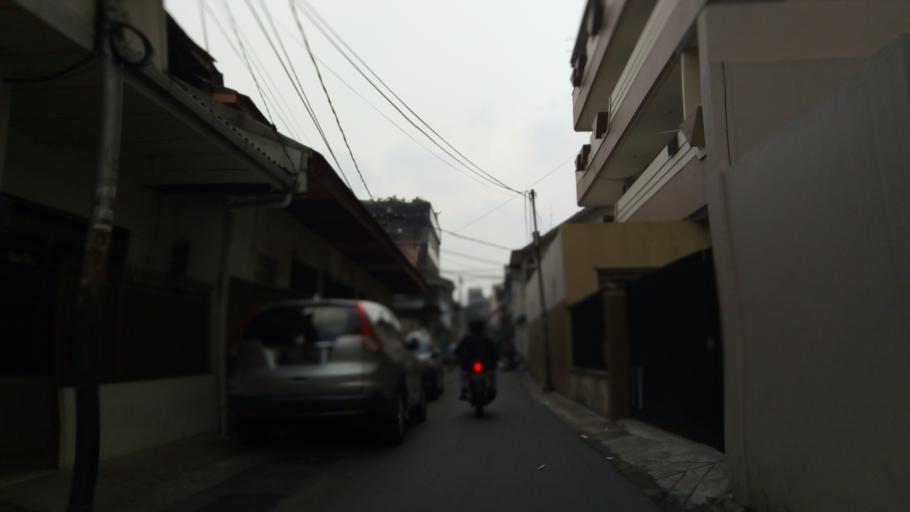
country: ID
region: Jakarta Raya
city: Jakarta
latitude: -6.1638
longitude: 106.8357
